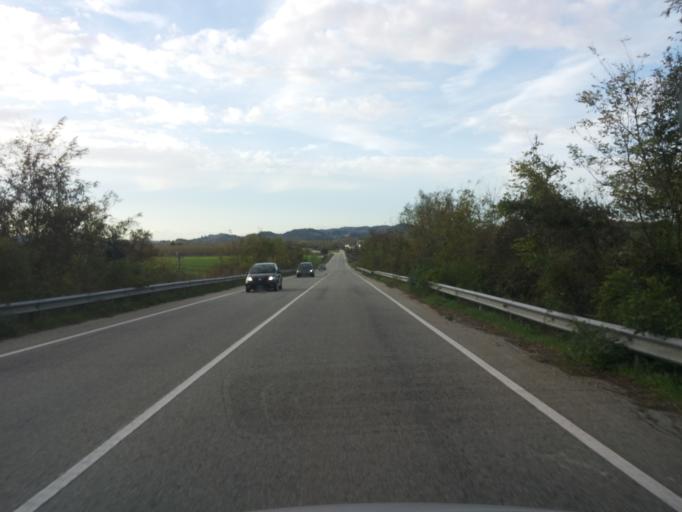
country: IT
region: Piedmont
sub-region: Provincia di Alessandria
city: Cereseto
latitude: 45.1092
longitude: 8.3329
